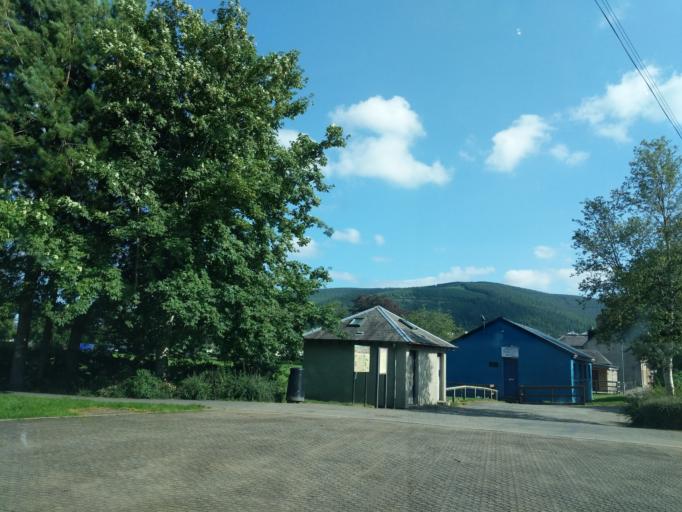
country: GB
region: Scotland
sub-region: The Scottish Borders
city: Innerleithen
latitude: 55.6195
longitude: -3.0676
